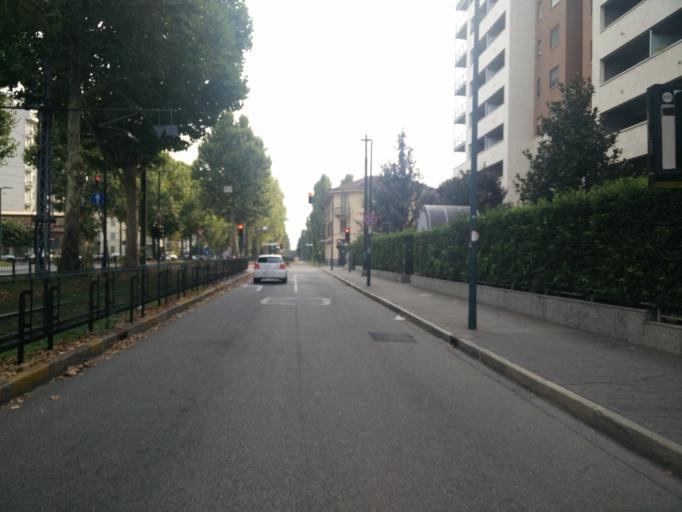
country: IT
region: Piedmont
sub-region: Provincia di Torino
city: Gerbido
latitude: 45.0291
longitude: 7.6420
